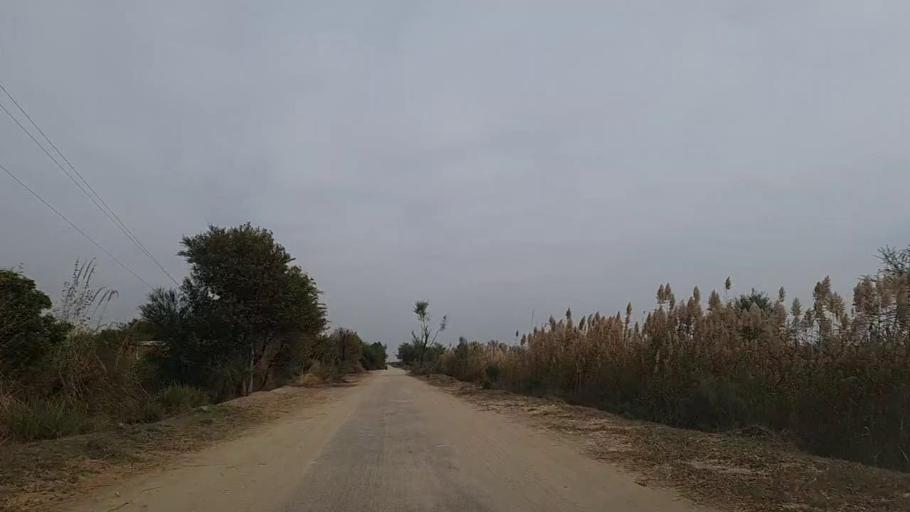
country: PK
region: Sindh
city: Jam Sahib
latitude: 26.4002
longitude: 68.5241
